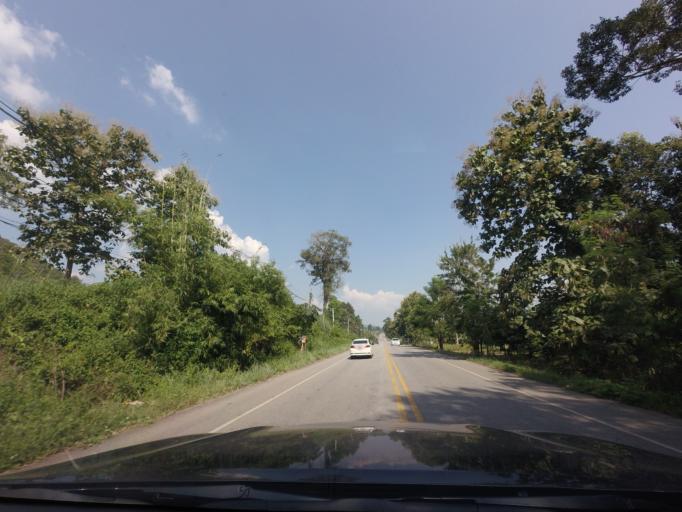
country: TH
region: Phitsanulok
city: Nakhon Thai
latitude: 17.1265
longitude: 100.7552
